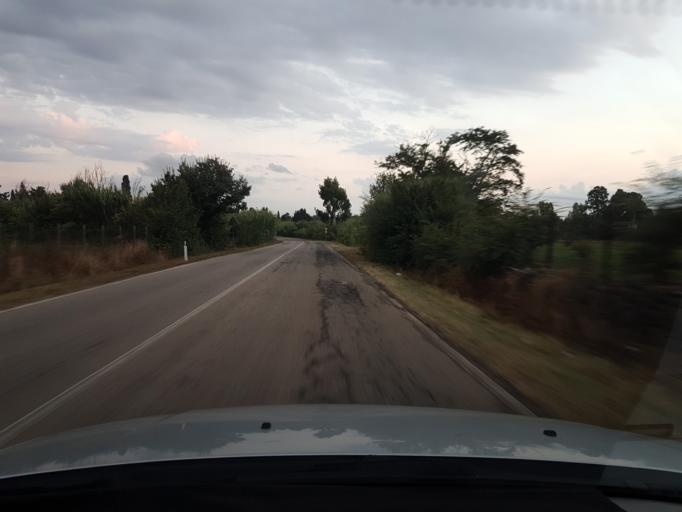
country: IT
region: Sardinia
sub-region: Provincia di Oristano
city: Milis
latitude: 40.0497
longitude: 8.6302
